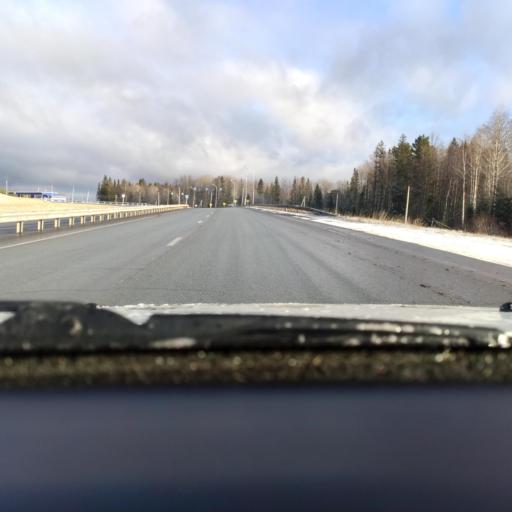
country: RU
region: Perm
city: Ferma
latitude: 57.9989
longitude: 56.3895
